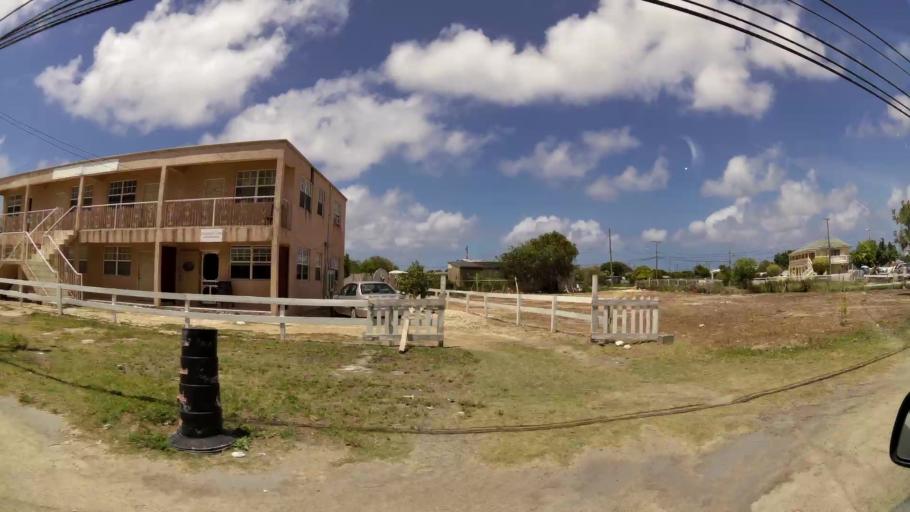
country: TC
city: Cockburn Town
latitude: 21.4618
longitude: -71.1397
